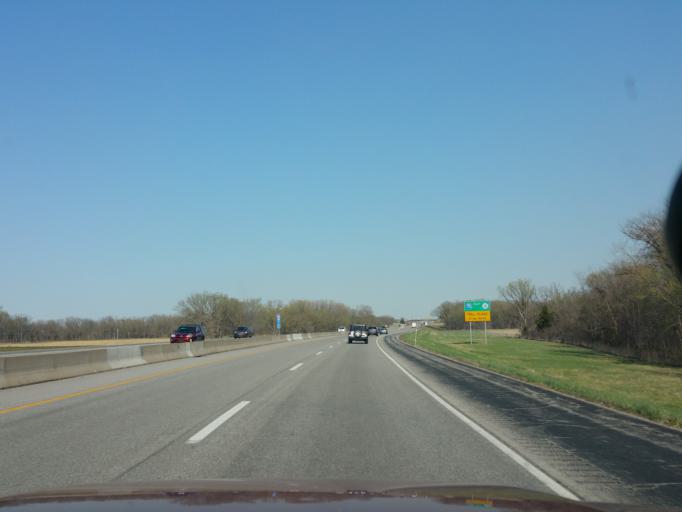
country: US
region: Kansas
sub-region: Leavenworth County
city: Tonganoxie
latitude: 39.0674
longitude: -95.0311
